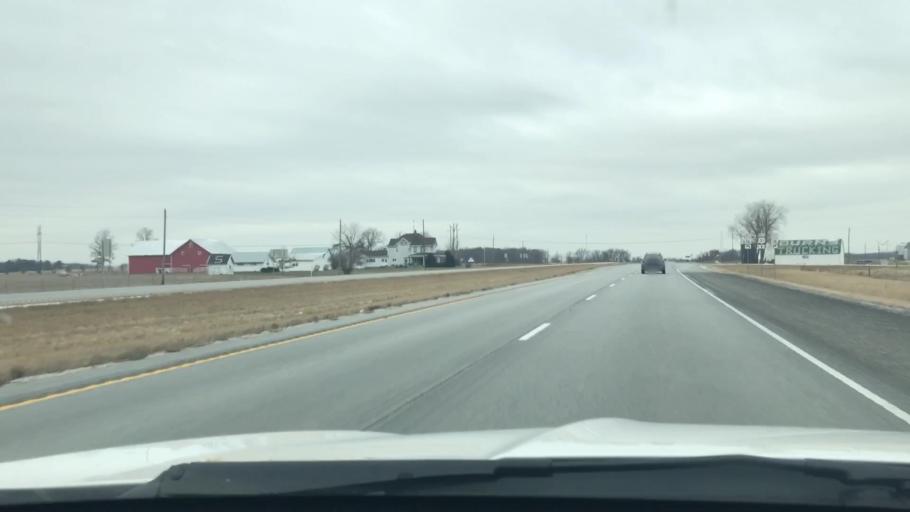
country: US
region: Indiana
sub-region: Miami County
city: Peru
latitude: 40.8636
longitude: -86.1357
